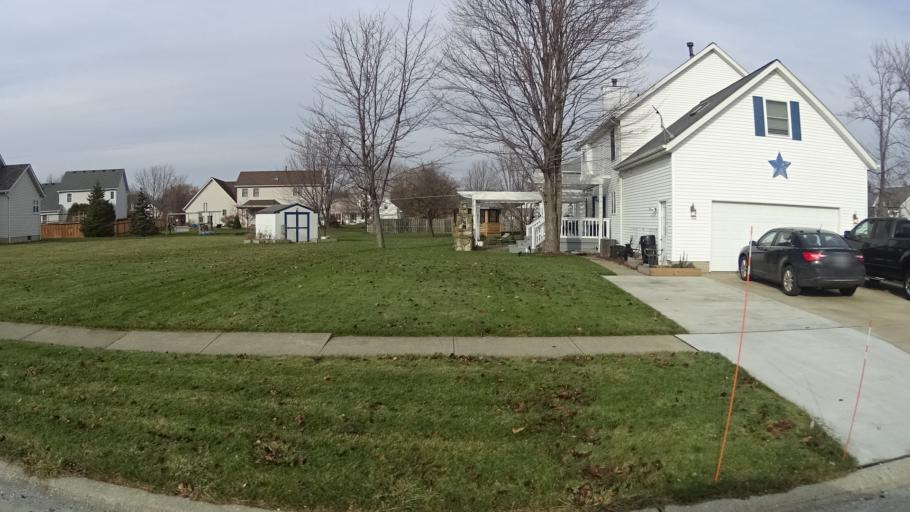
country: US
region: Ohio
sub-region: Lorain County
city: Amherst
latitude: 41.4062
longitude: -82.2448
